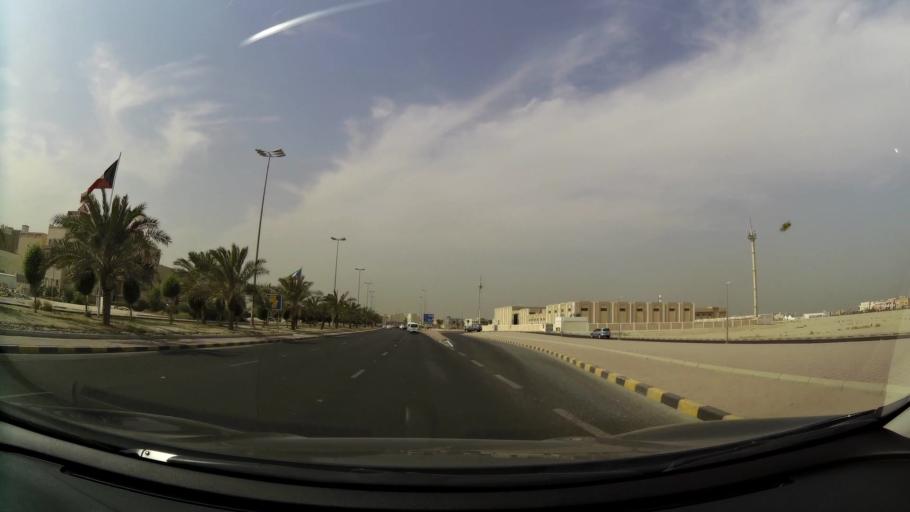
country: KW
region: Al Farwaniyah
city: Janub as Surrah
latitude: 29.2847
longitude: 48.0051
